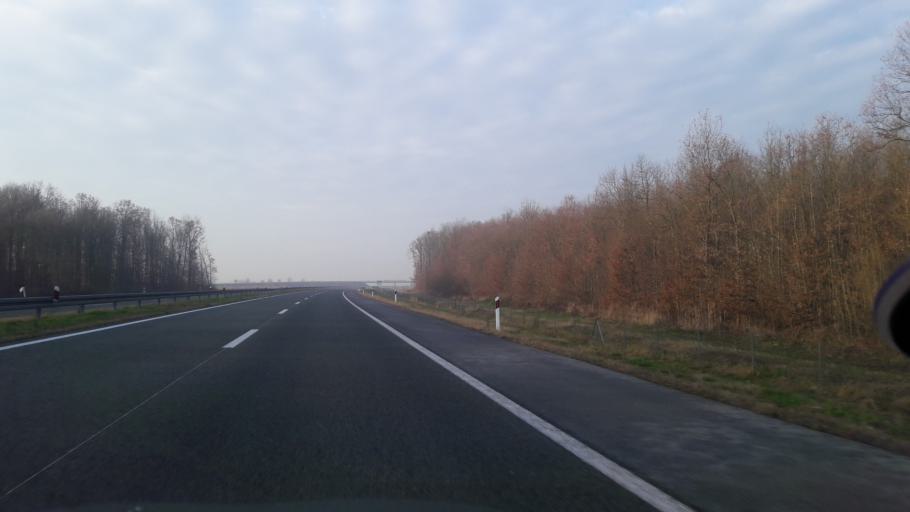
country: HR
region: Osjecko-Baranjska
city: Vuka
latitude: 45.4148
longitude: 18.4441
